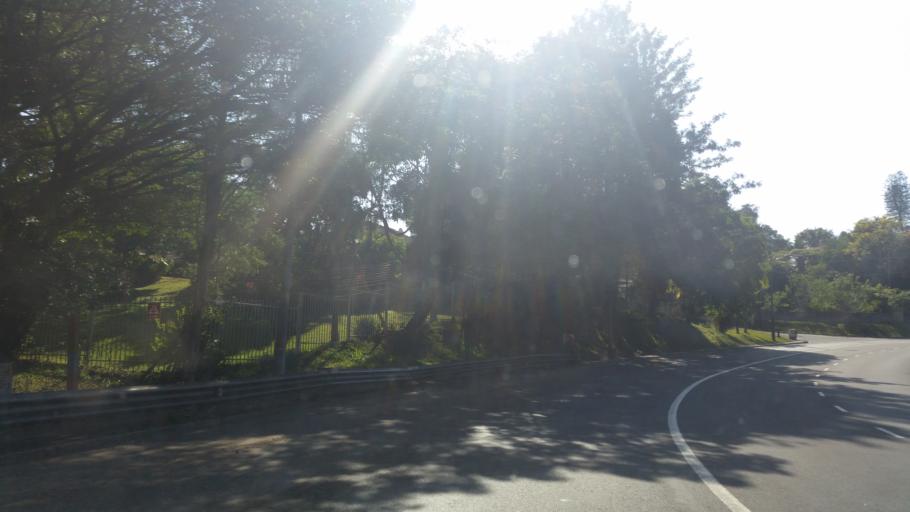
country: ZA
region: KwaZulu-Natal
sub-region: eThekwini Metropolitan Municipality
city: Berea
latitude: -29.8306
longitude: 30.9106
